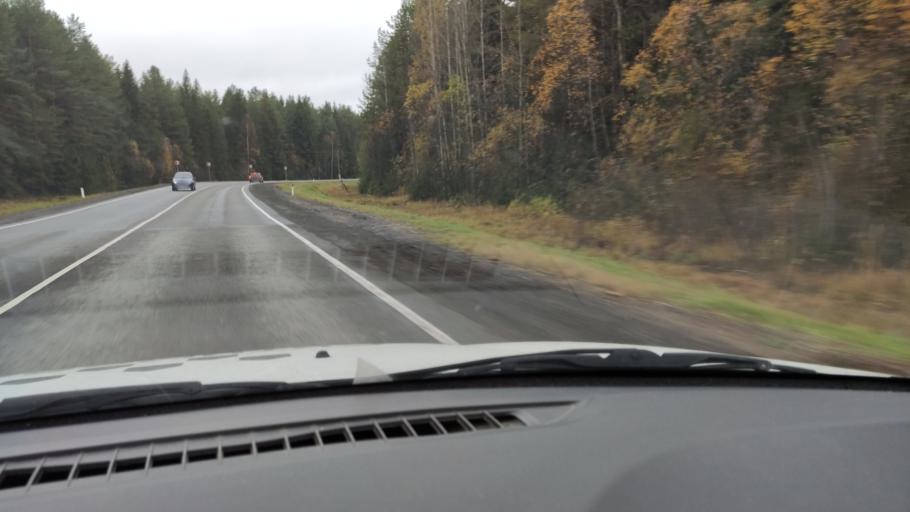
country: RU
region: Kirov
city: Belaya Kholunitsa
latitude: 58.8792
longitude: 50.8701
